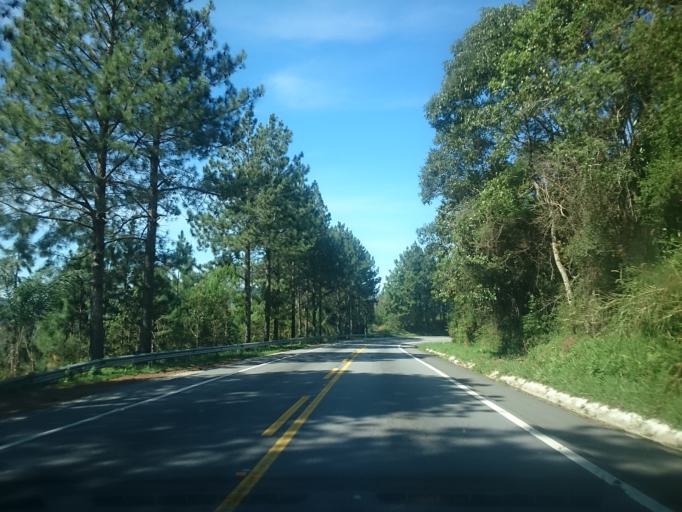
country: BR
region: Santa Catarina
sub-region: Santo Amaro Da Imperatriz
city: Santo Amaro da Imperatriz
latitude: -27.6957
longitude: -48.9657
